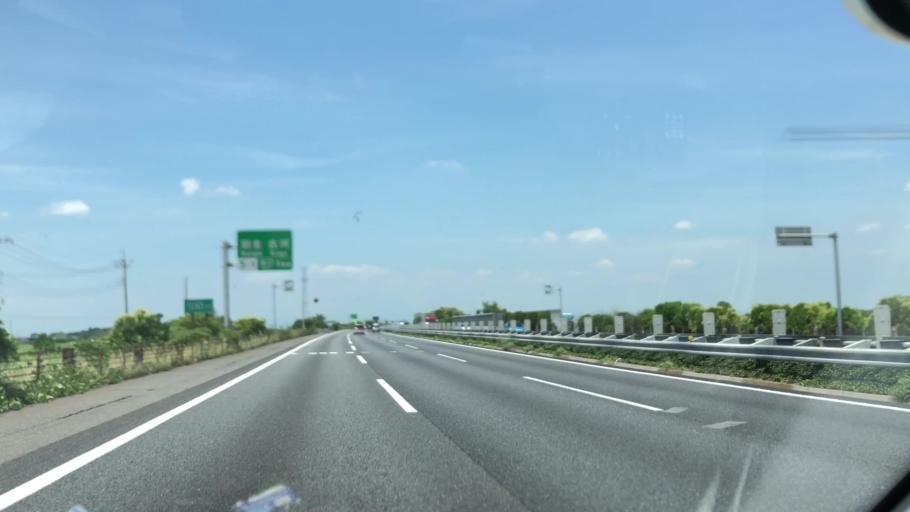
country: JP
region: Saitama
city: Kazo
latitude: 36.1593
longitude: 139.5926
